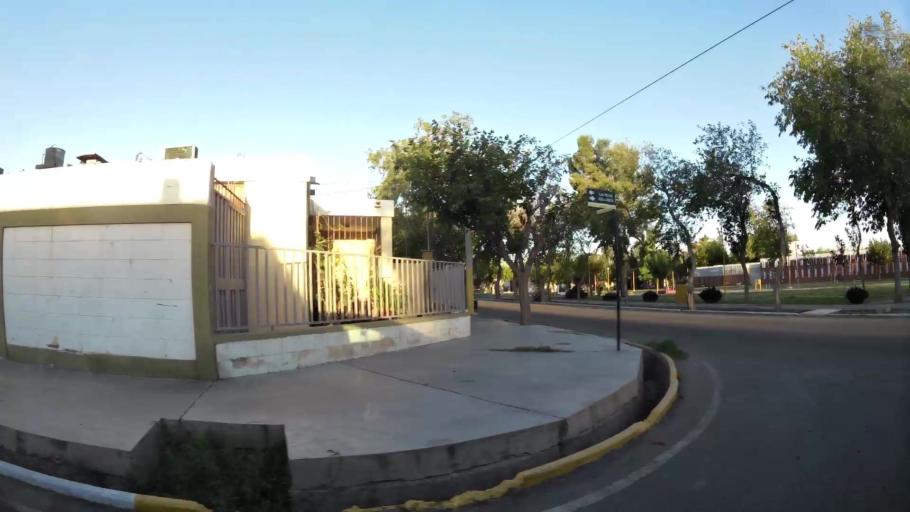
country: AR
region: San Juan
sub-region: Departamento de Santa Lucia
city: Santa Lucia
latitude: -31.5263
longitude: -68.5067
